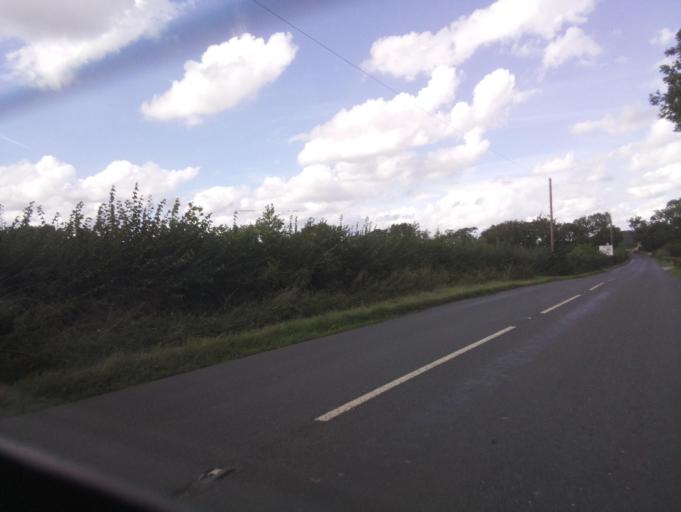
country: GB
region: England
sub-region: North Yorkshire
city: Leyburn
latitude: 54.2768
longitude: -1.7795
